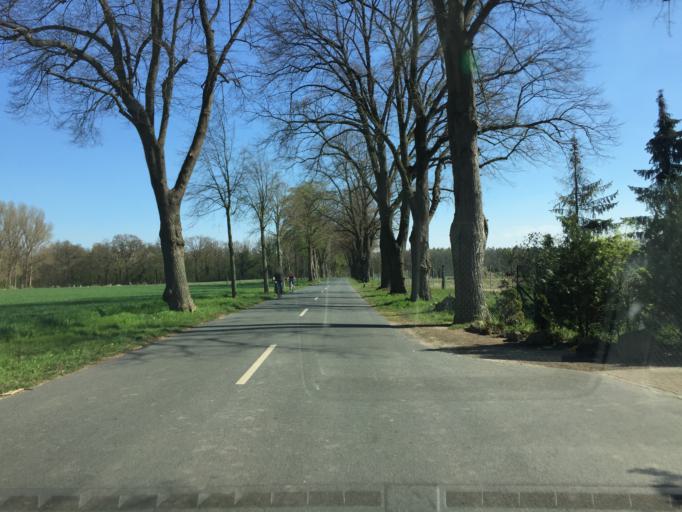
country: DE
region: Lower Saxony
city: Gross Munzel
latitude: 52.4190
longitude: 9.4974
